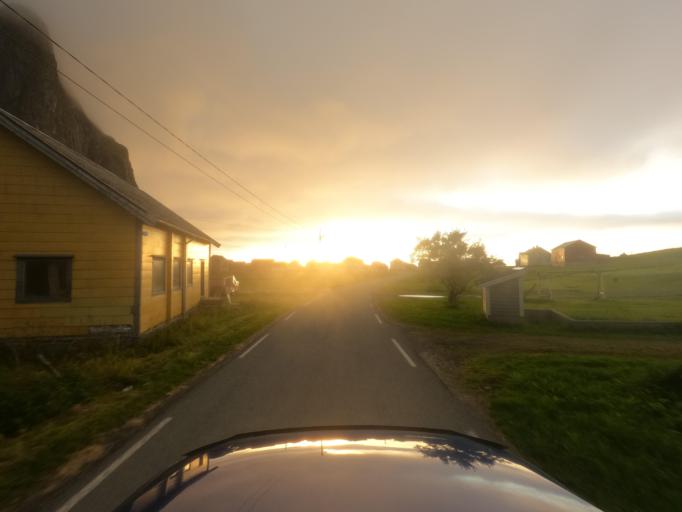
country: NO
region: Nordland
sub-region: Vestvagoy
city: Evjen
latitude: 68.3073
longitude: 13.6883
